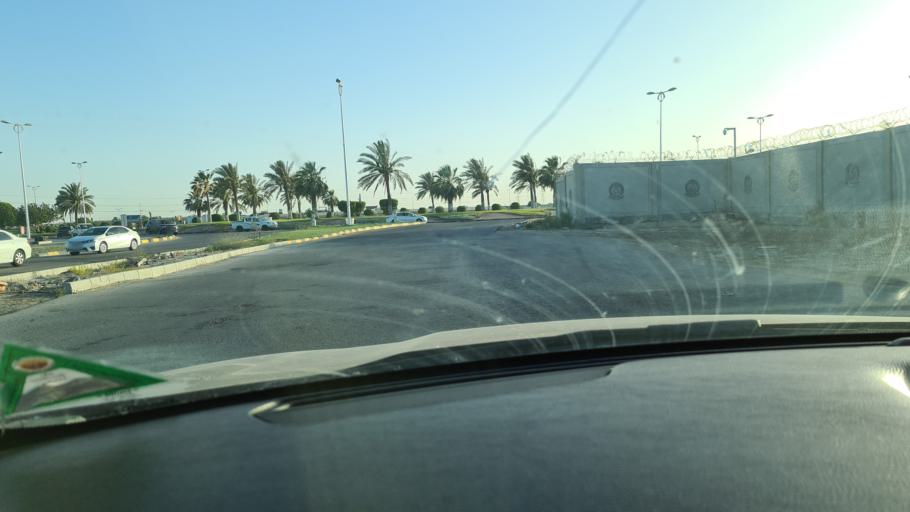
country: SA
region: Eastern Province
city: Al Jubayl
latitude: 26.9278
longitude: 49.7126
